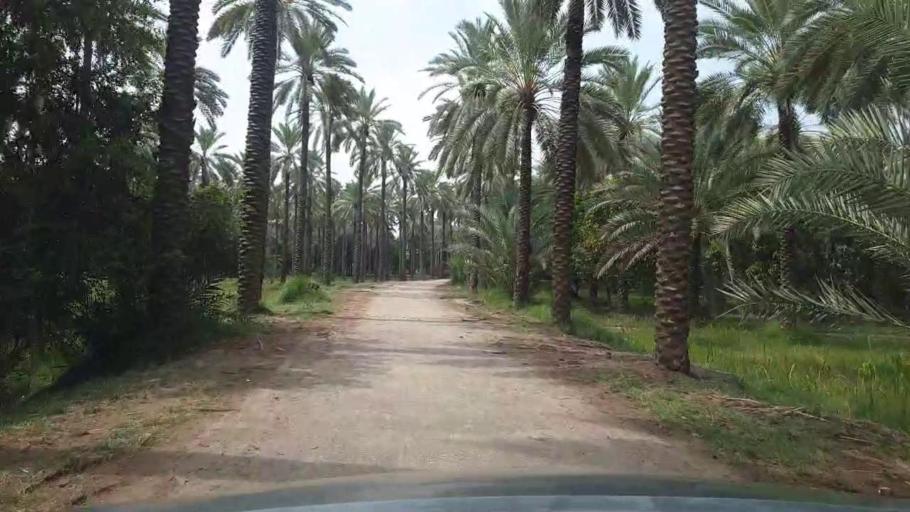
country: PK
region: Sindh
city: Pir jo Goth
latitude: 27.6151
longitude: 68.6756
